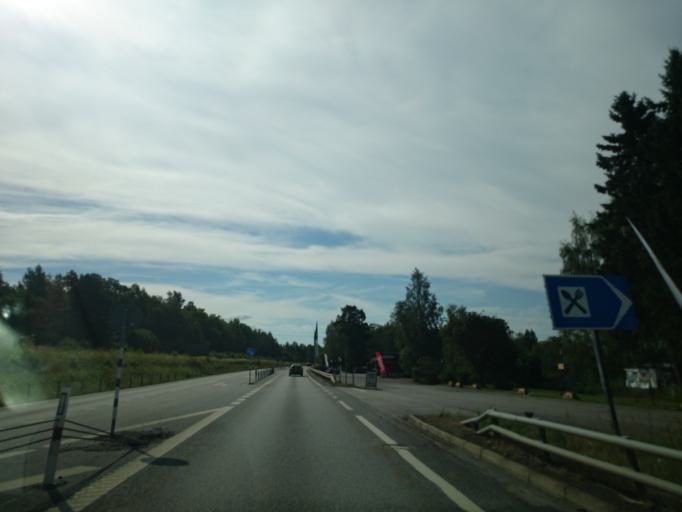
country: SE
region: Kalmar
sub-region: Vasterviks Kommun
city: Vaestervik
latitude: 57.7982
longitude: 16.5154
